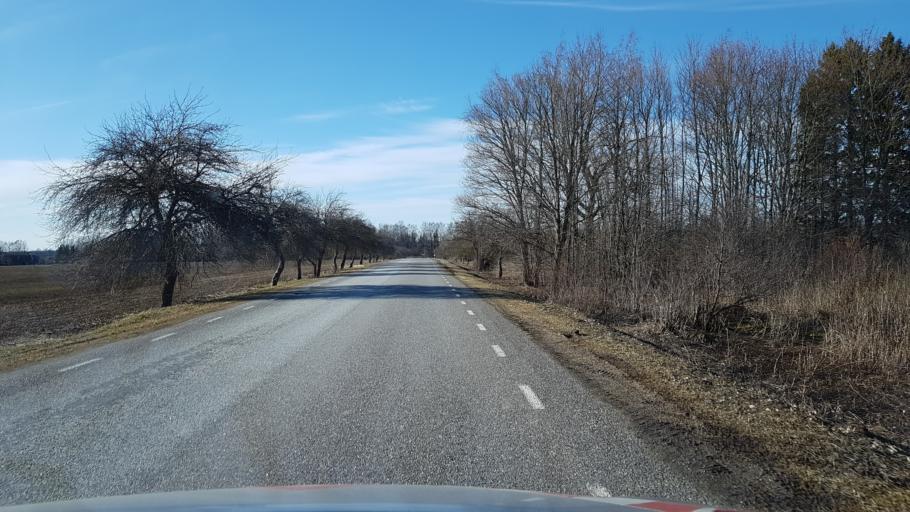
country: EE
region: Laeaene-Virumaa
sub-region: Kadrina vald
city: Kadrina
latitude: 59.3337
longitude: 26.1295
